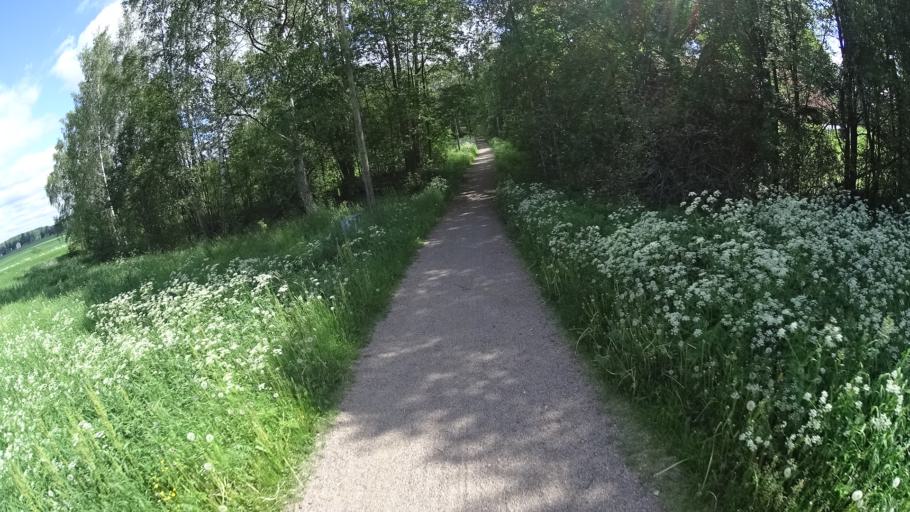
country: FI
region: Uusimaa
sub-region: Helsinki
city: Vantaa
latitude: 60.2366
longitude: 25.1311
